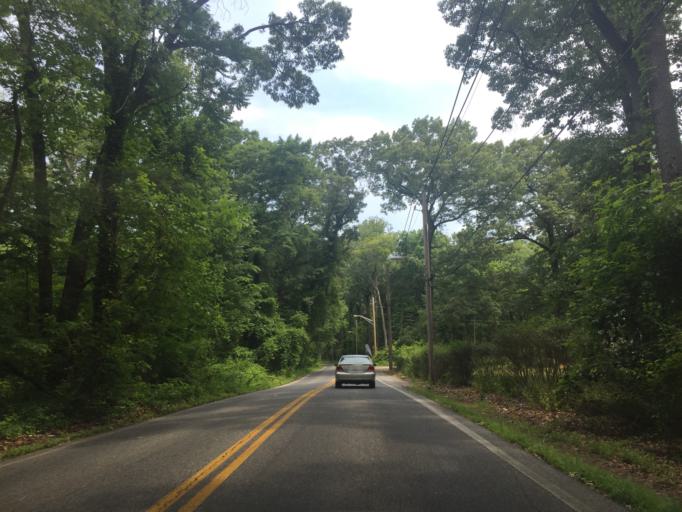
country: US
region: Maryland
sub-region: Baltimore County
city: Towson
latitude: 39.3723
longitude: -76.5790
